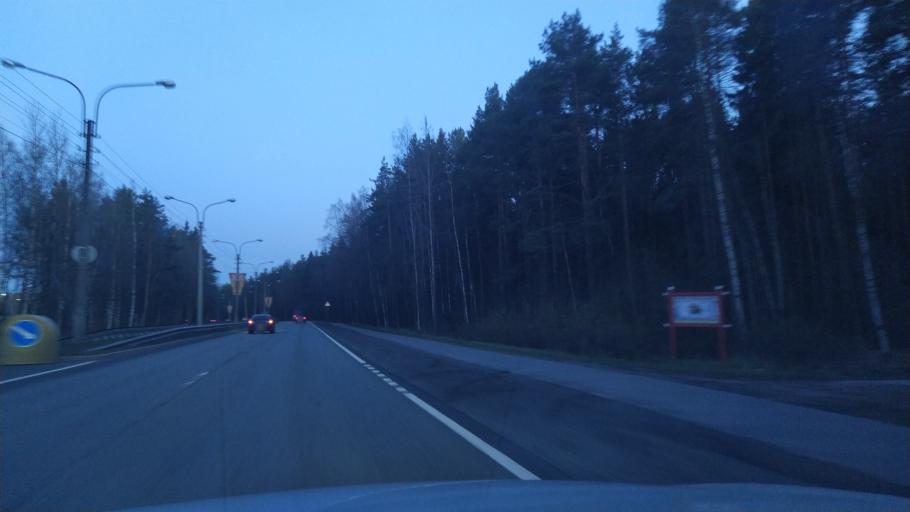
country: RU
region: St.-Petersburg
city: Tarkhovka
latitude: 60.0642
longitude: 29.9714
